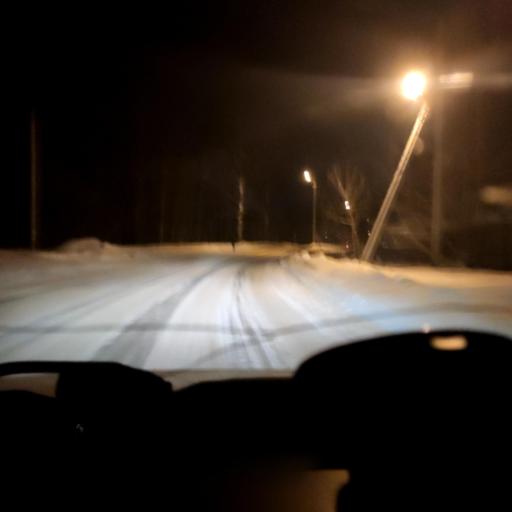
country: RU
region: Perm
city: Krasnokamsk
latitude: 58.0969
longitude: 55.7587
